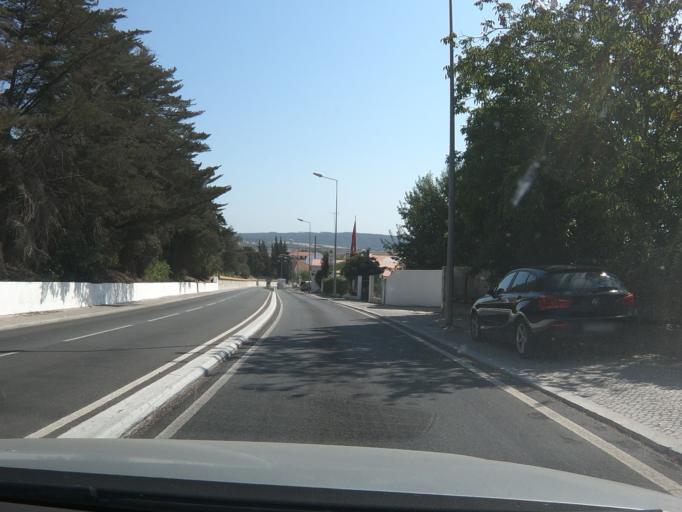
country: PT
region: Setubal
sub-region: Alcacer do Sal
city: Alcacer do Sal
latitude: 38.3728
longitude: -8.5080
